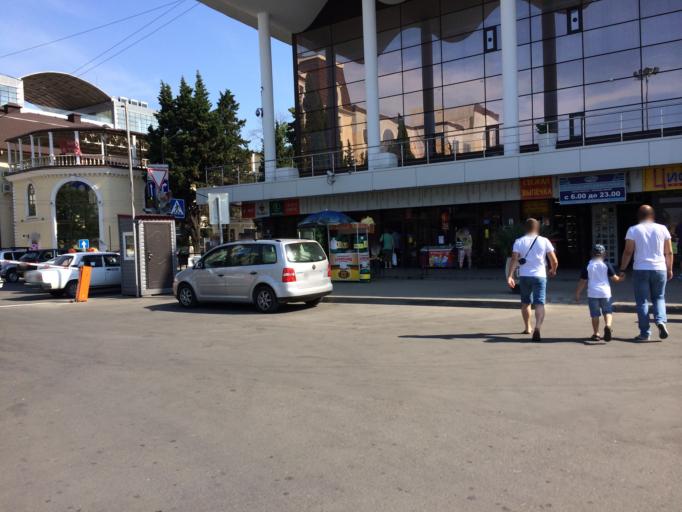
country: RU
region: Krasnodarskiy
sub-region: Sochi City
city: Sochi
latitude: 43.5926
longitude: 39.7280
